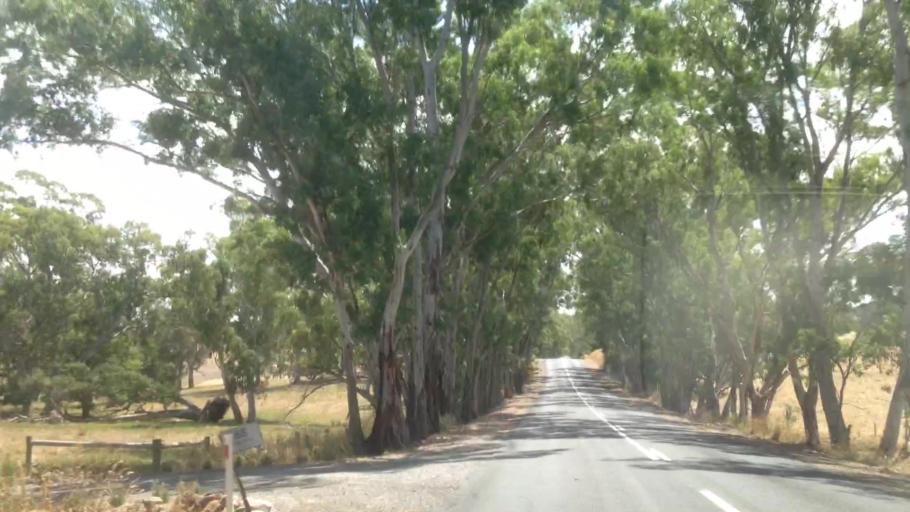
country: AU
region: South Australia
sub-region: Adelaide Hills
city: Birdwood
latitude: -34.7912
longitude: 138.9622
